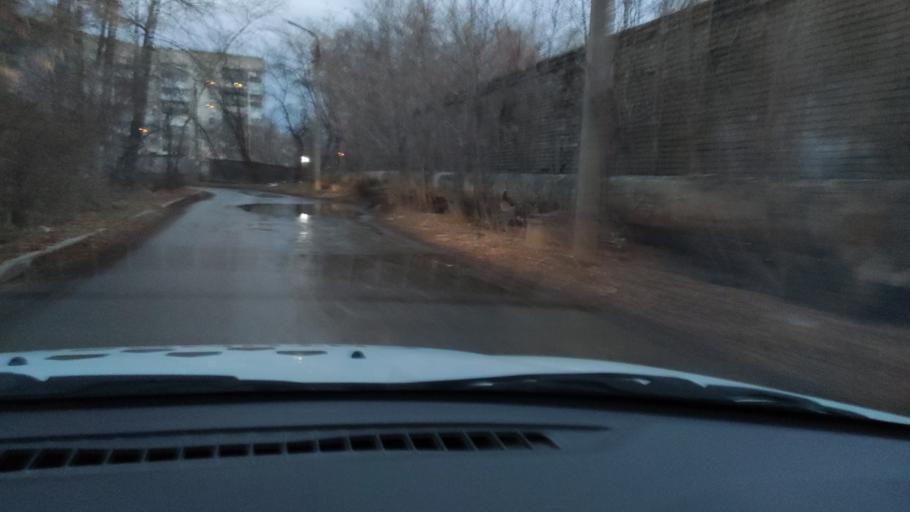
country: RU
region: Perm
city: Perm
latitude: 57.9696
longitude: 56.2709
